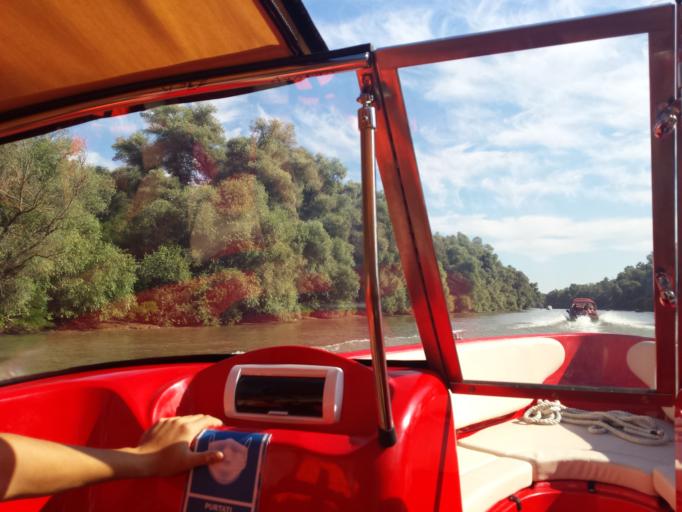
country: RO
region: Tulcea
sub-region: Comuna Nufaru
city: Nufaru
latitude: 45.2204
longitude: 28.8794
